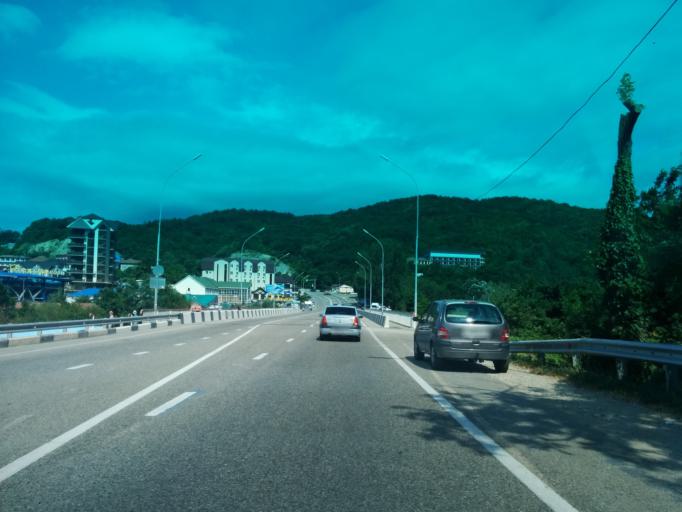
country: RU
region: Krasnodarskiy
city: Nebug
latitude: 44.1647
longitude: 39.0018
